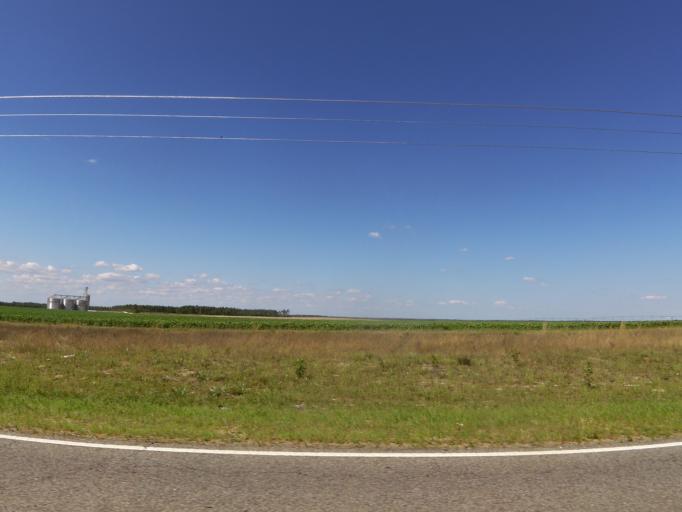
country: US
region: South Carolina
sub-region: Aiken County
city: New Ellenton
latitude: 33.5096
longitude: -81.5568
